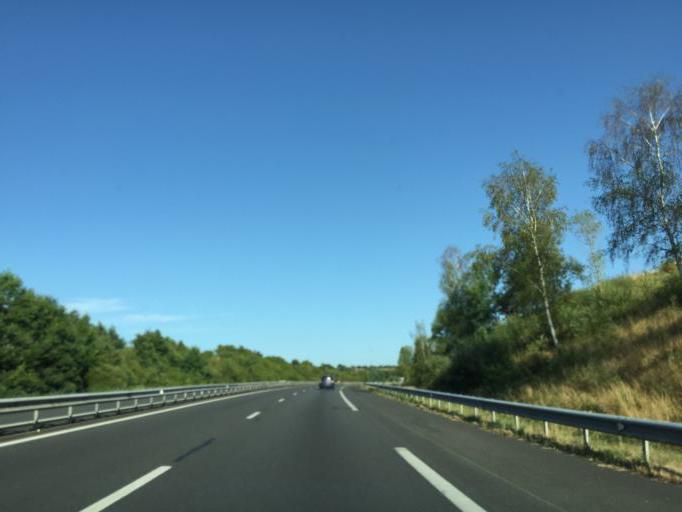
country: FR
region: Auvergne
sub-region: Departement de l'Allier
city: Montmarault
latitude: 46.3310
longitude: 2.9043
